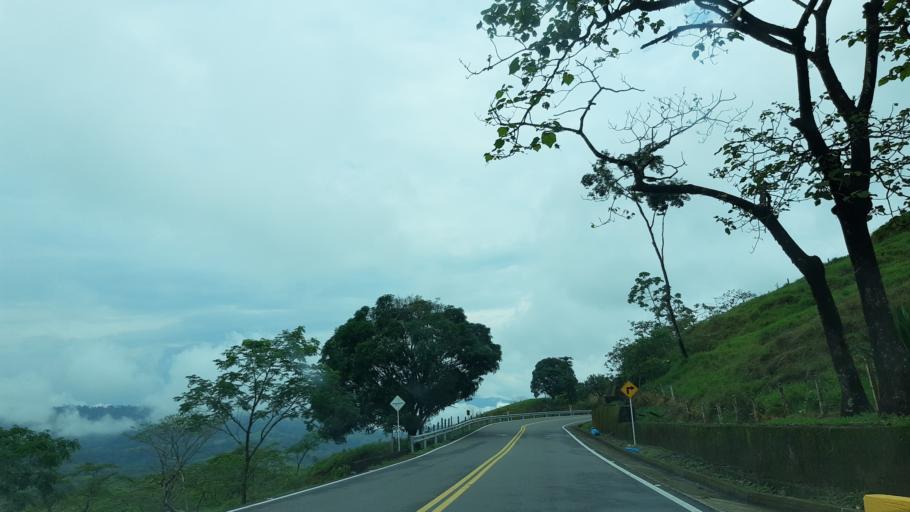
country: CO
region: Casanare
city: Sabanalarga
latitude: 4.7908
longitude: -73.0537
